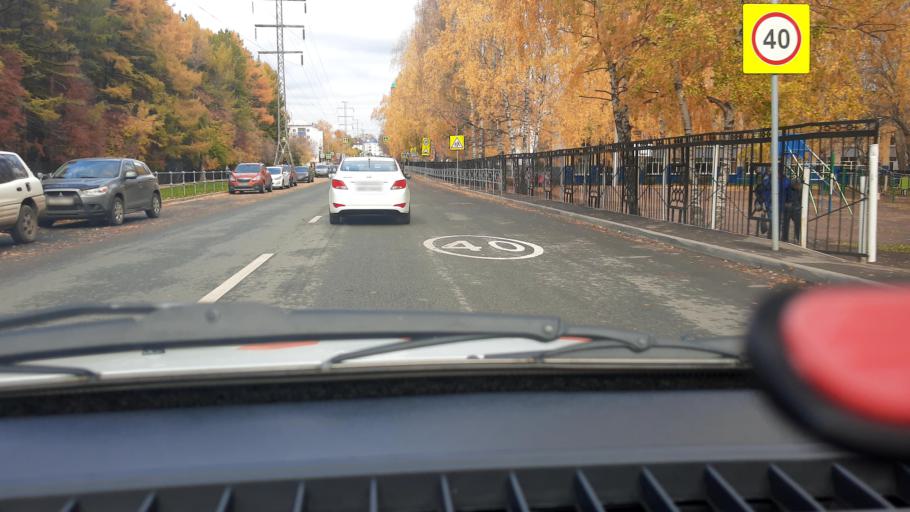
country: RU
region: Bashkortostan
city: Ufa
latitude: 54.7663
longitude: 56.0237
